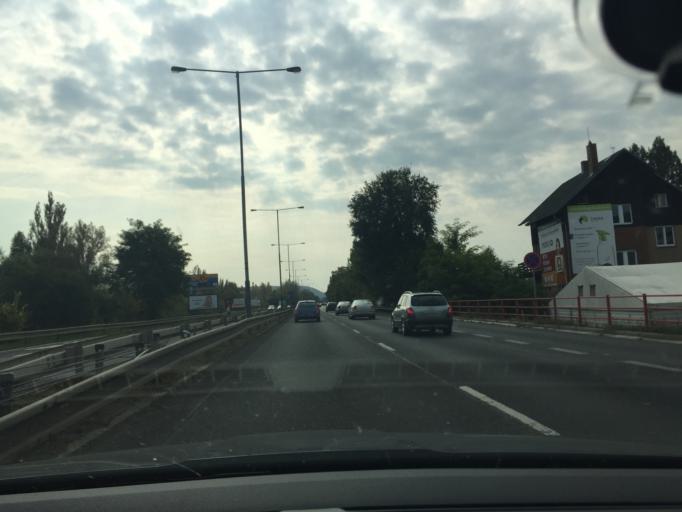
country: CZ
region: Praha
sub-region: Praha 12
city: Modrany
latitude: 50.0121
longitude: 14.3942
